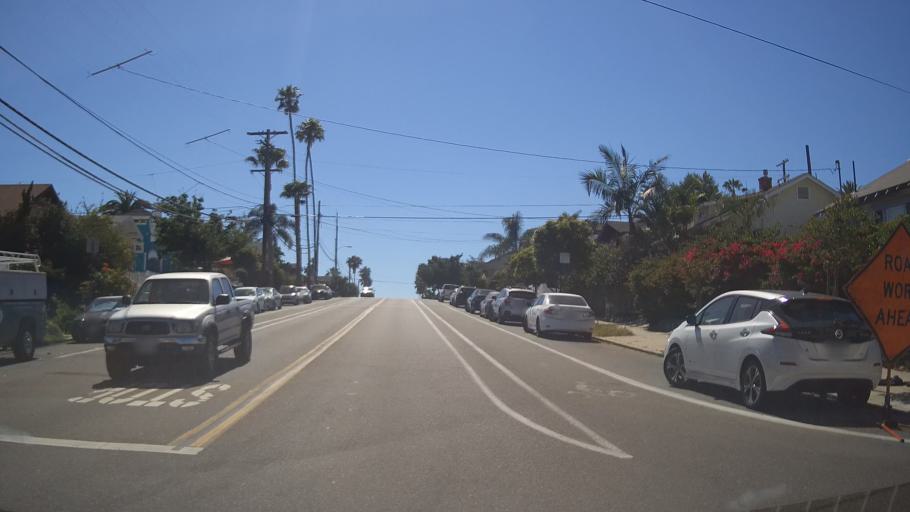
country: US
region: California
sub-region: San Diego County
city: San Diego
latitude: 32.7610
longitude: -117.1438
